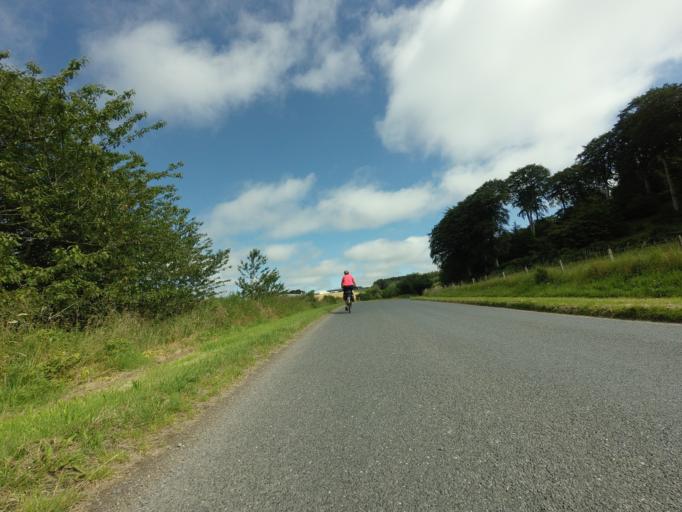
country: GB
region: Scotland
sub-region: Aberdeenshire
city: Turriff
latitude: 57.5637
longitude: -2.4940
